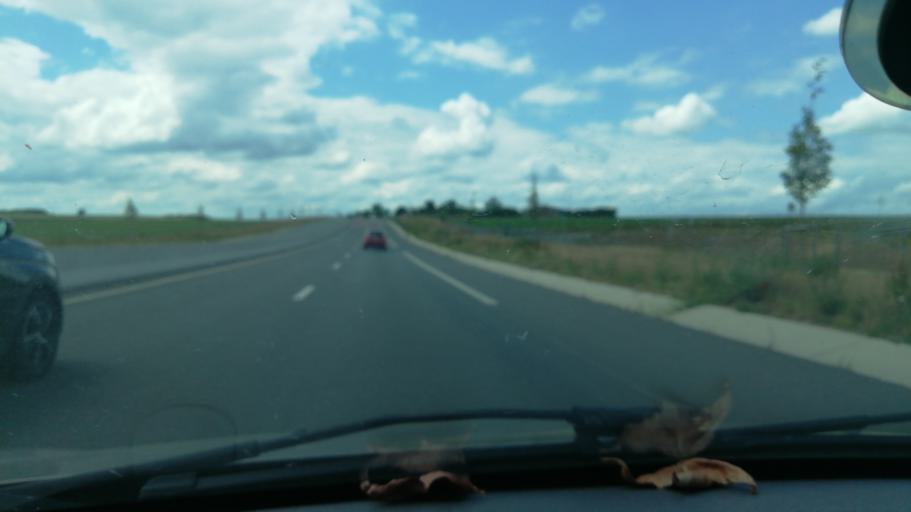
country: FR
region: Nord-Pas-de-Calais
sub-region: Departement du Pas-de-Calais
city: Aubigny-en-Artois
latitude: 50.3410
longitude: 2.6010
